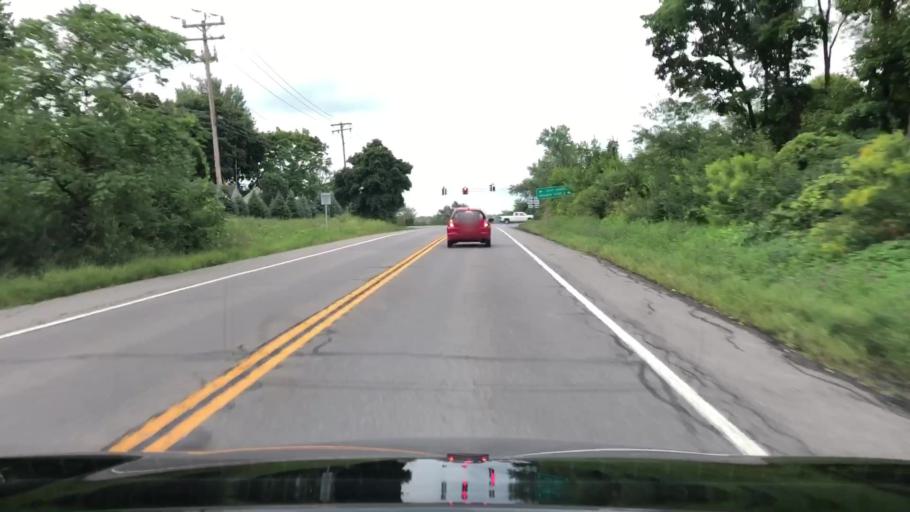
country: US
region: New York
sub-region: Erie County
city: Orchard Park
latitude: 42.7699
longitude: -78.6969
